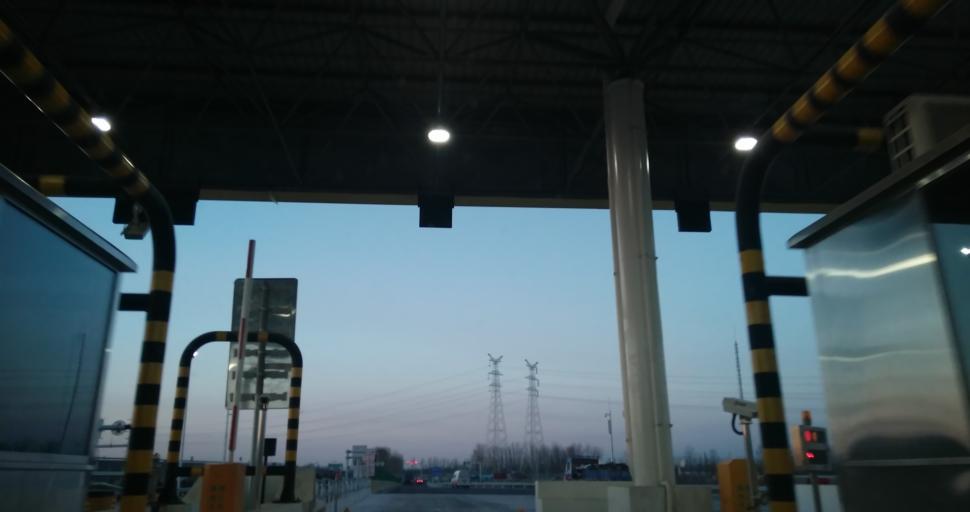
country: CN
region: Beijing
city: Qingyundian
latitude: 39.6814
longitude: 116.4516
